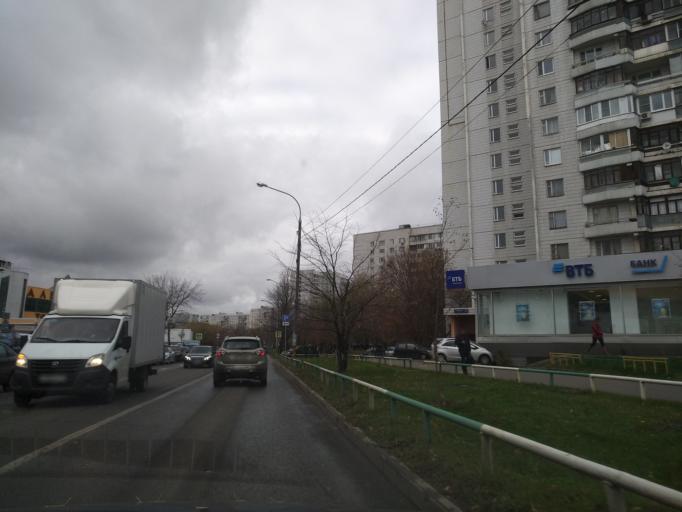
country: RU
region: Moscow
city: Bibirevo
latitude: 55.8850
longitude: 37.6048
